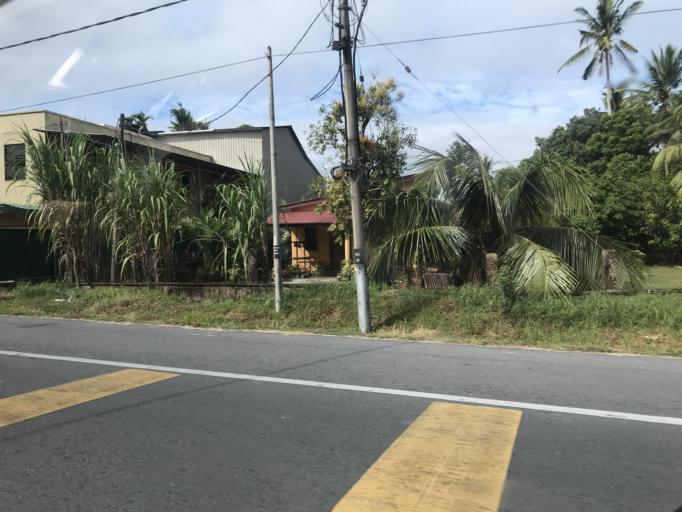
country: MY
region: Kelantan
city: Kota Bharu
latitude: 6.1228
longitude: 102.1851
